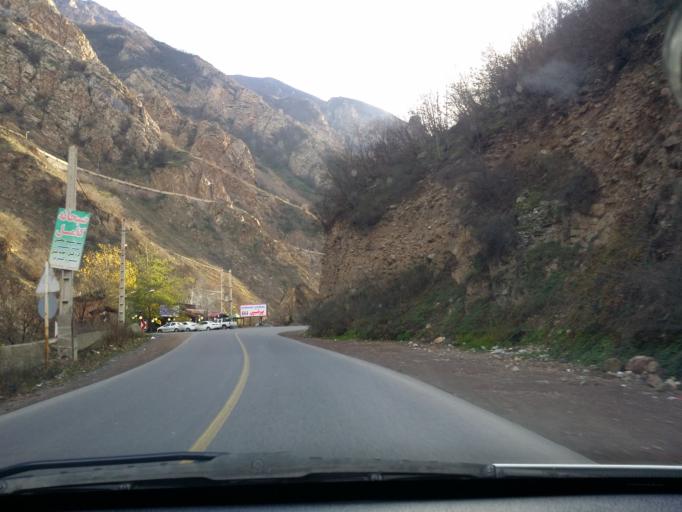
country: IR
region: Mazandaran
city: Chalus
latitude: 36.2649
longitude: 51.2594
